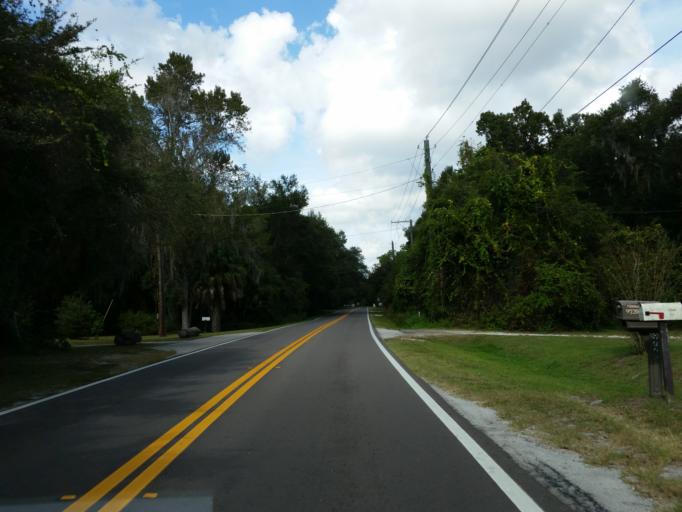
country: US
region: Florida
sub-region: Hillsborough County
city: Riverview
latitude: 27.8585
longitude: -82.3197
